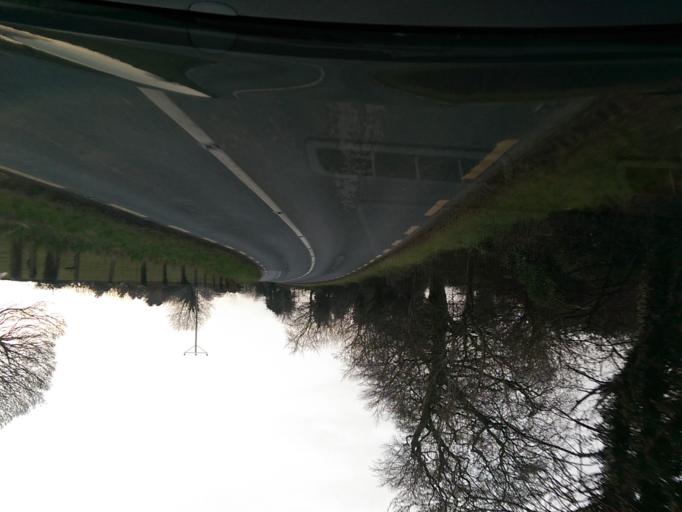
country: IE
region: Leinster
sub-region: An Longfort
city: Ballymahon
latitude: 53.5005
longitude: -7.8436
